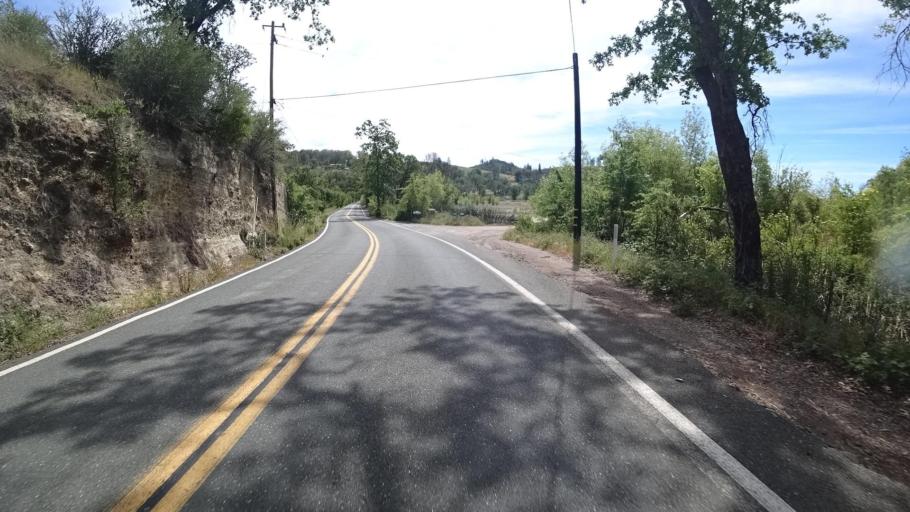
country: US
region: California
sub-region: Lake County
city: Cobb
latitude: 38.8758
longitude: -122.6806
